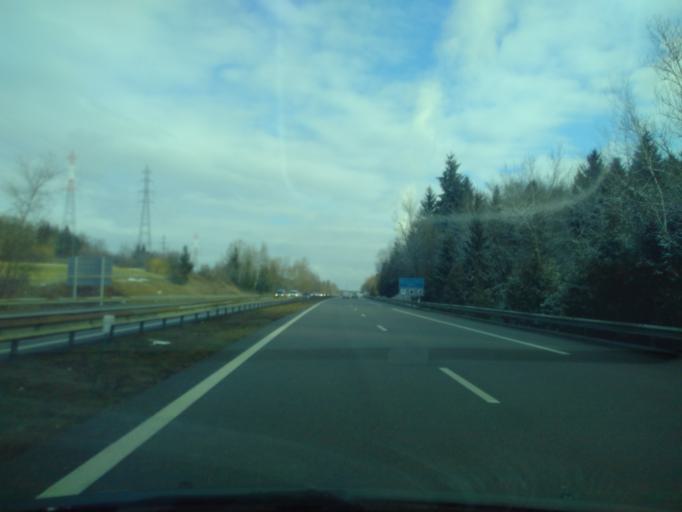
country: FR
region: Rhone-Alpes
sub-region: Departement de la Haute-Savoie
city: Chavanod
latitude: 45.8685
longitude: 6.0617
